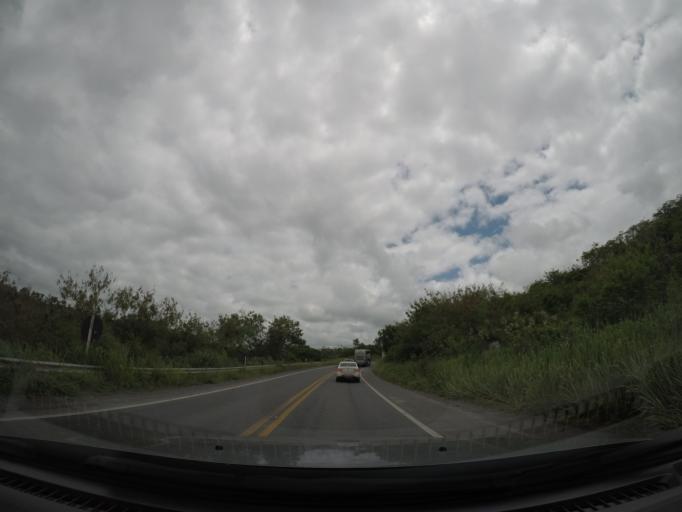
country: BR
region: Bahia
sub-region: Ruy Barbosa
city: Terra Nova
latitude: -12.4590
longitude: -40.5753
